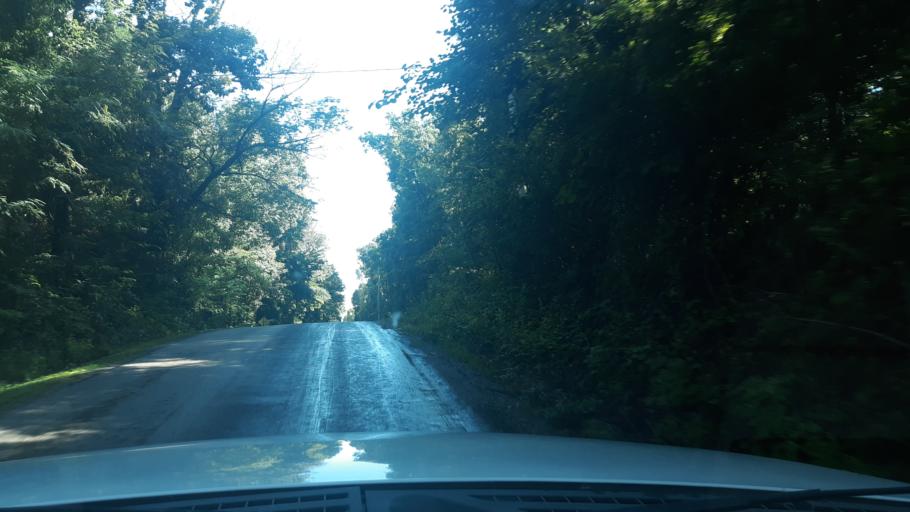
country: US
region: Illinois
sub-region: Saline County
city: Harrisburg
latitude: 37.8515
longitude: -88.5814
